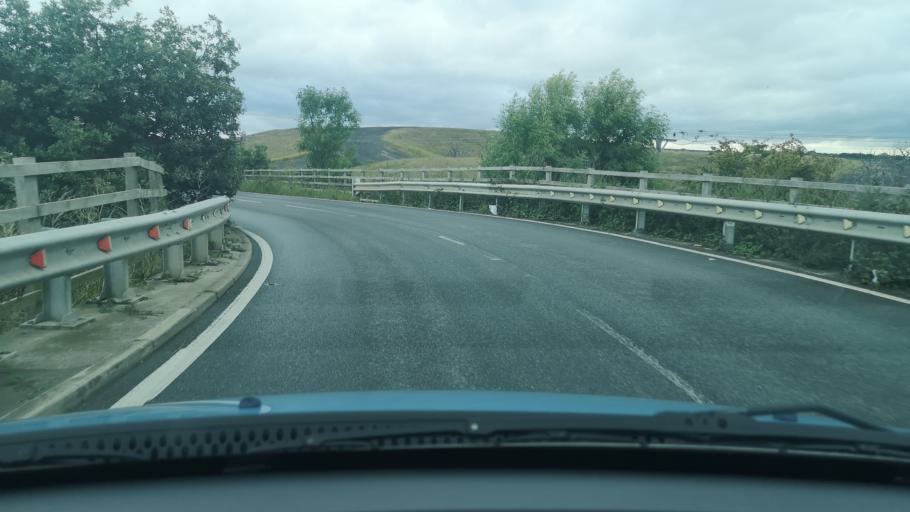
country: GB
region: England
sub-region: Doncaster
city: Hatfield
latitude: 53.6004
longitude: -0.9932
